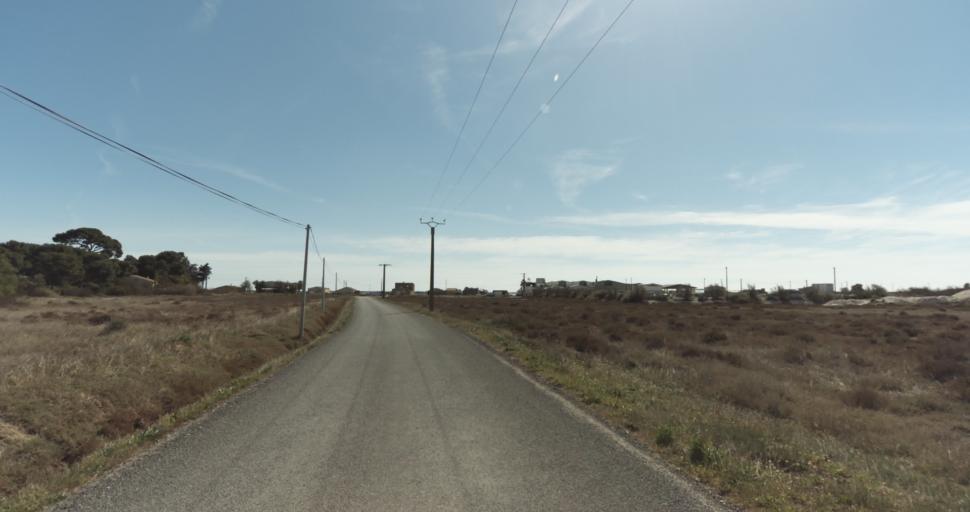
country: FR
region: Languedoc-Roussillon
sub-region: Departement de l'Herault
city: Marseillan
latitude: 43.3836
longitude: 3.5536
